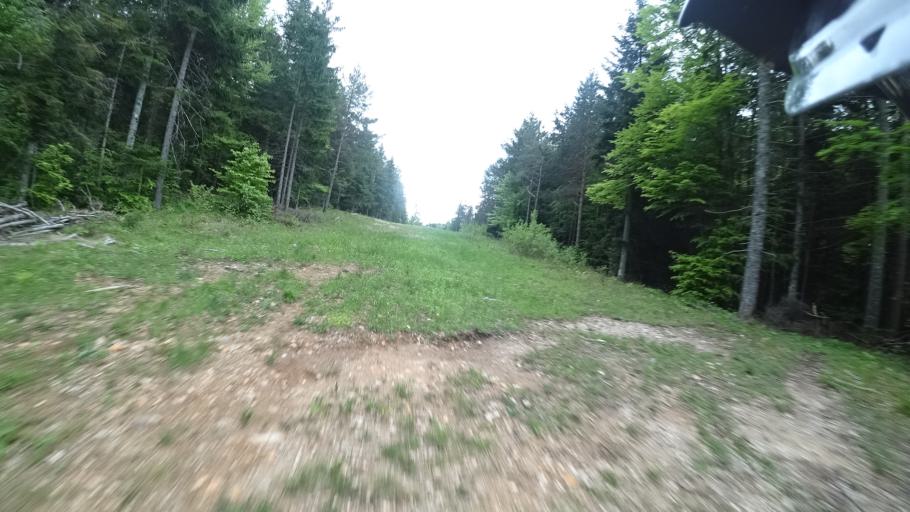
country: HR
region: Licko-Senjska
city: Jezerce
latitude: 44.8828
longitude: 15.4310
